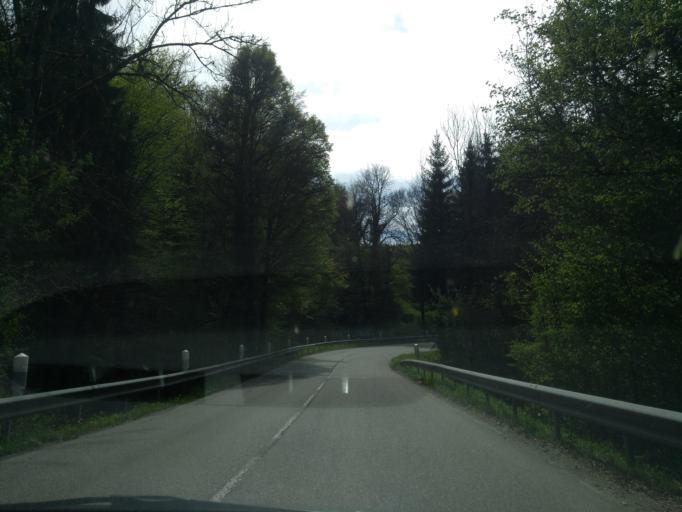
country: FR
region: Rhone-Alpes
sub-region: Departement de la Haute-Savoie
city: Chavanod
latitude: 45.8783
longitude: 6.0344
